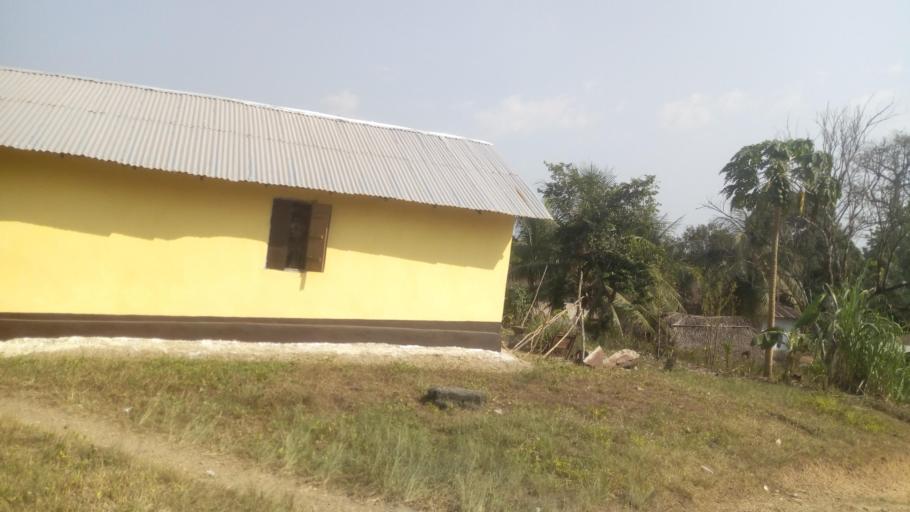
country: SL
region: Southern Province
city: Mogbwemo
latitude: 7.6106
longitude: -12.1812
